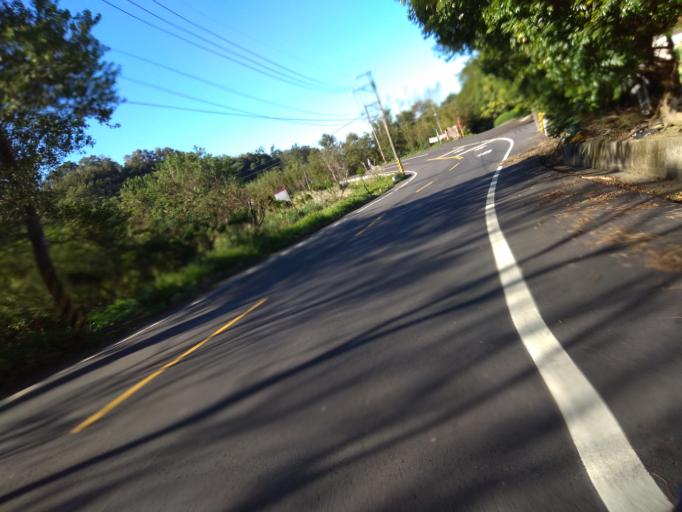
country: TW
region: Taiwan
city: Daxi
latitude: 24.8646
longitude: 121.1554
